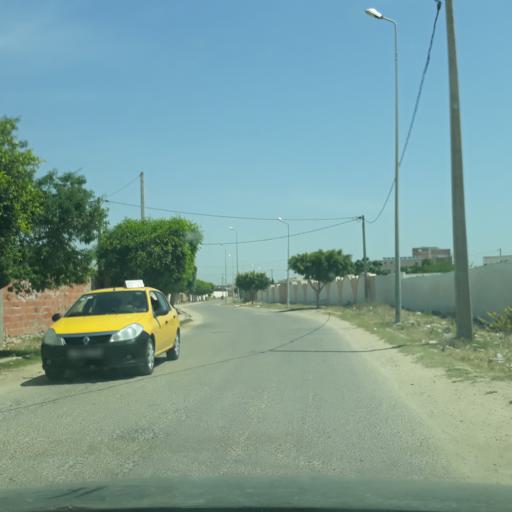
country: TN
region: Safaqis
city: Al Qarmadah
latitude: 34.8236
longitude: 10.7816
